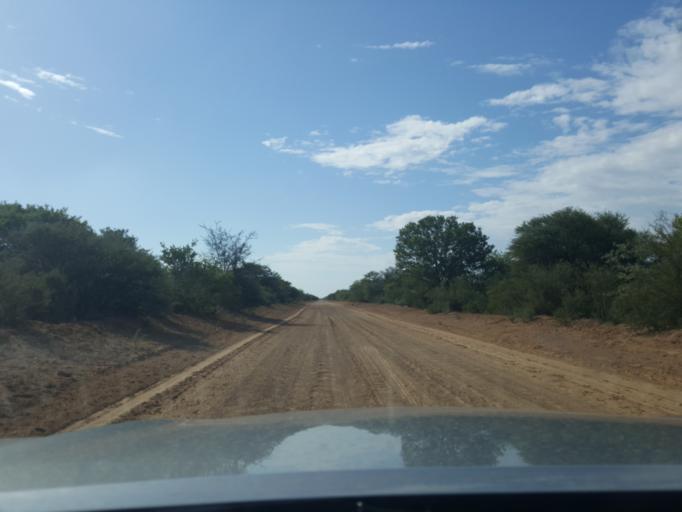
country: BW
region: Kweneng
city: Khudumelapye
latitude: -23.5109
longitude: 24.7128
